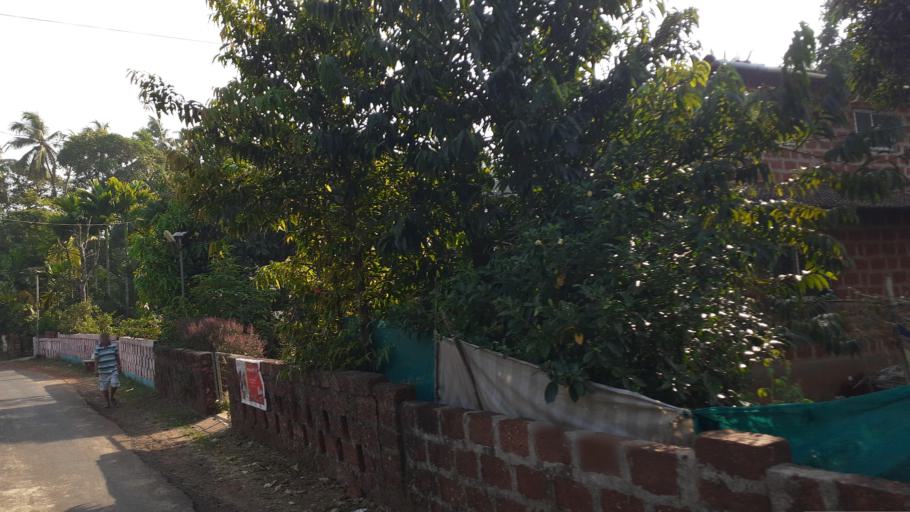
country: IN
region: Maharashtra
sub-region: Ratnagiri
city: Ratnagiri
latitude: 17.2151
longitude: 73.2479
